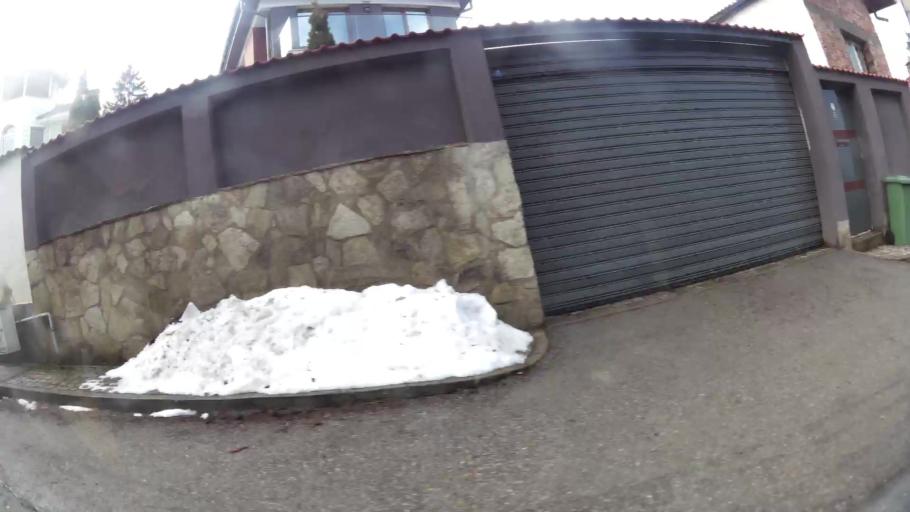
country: BG
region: Sofia-Capital
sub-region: Stolichna Obshtina
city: Sofia
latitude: 42.6447
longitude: 23.2775
